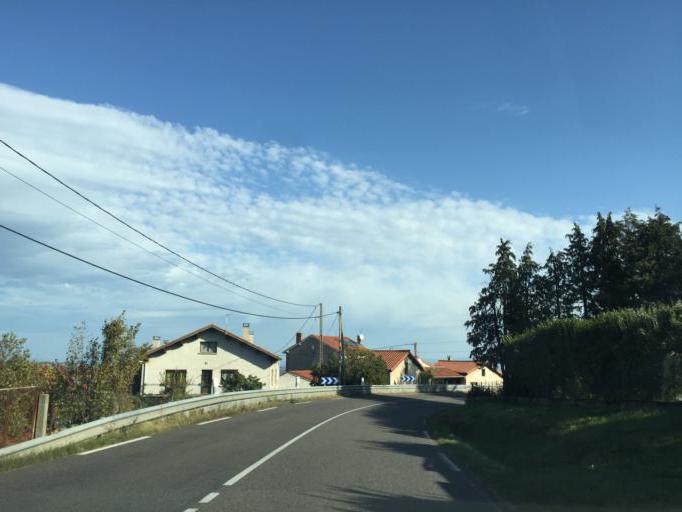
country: FR
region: Rhone-Alpes
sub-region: Departement de la Loire
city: Perigneux
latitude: 45.4626
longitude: 4.1169
